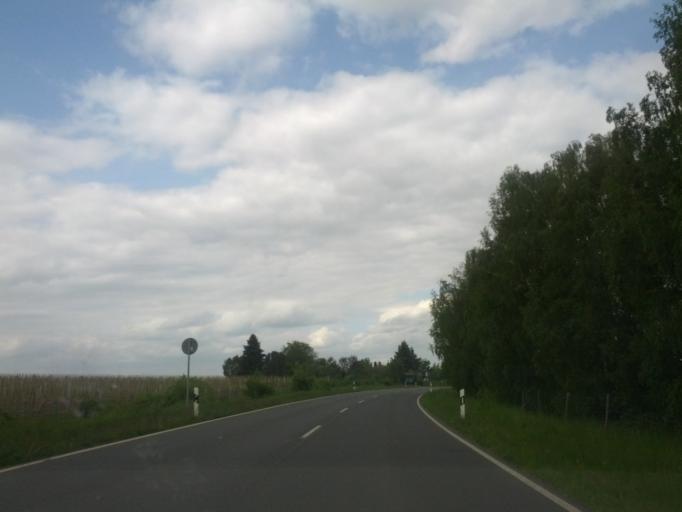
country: DE
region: Saxony
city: Kreischa
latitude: 50.9647
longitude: 13.7990
